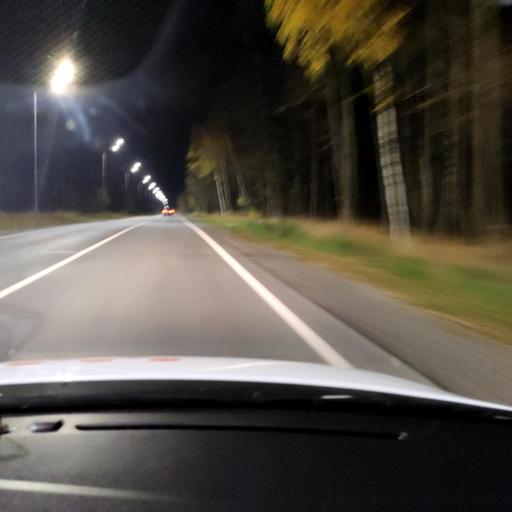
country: RU
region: Tatarstan
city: Stolbishchi
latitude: 55.6333
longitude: 49.0975
